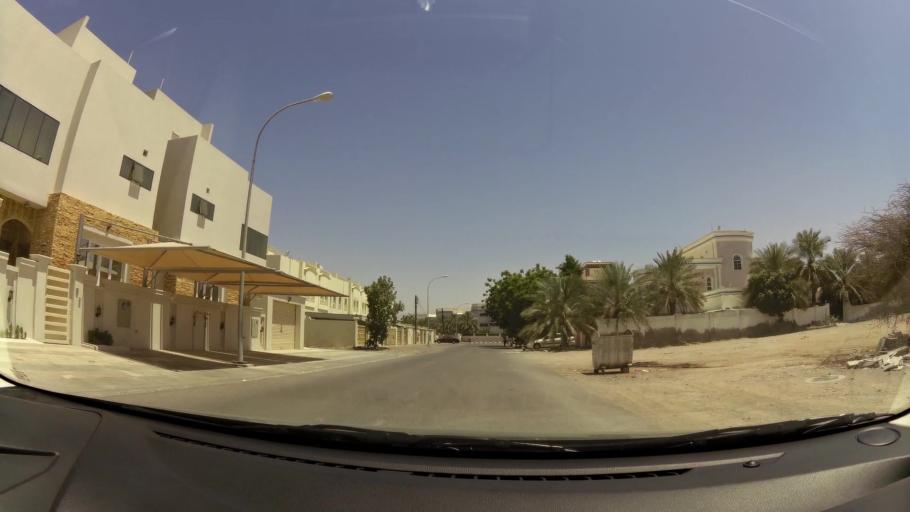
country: OM
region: Muhafazat Masqat
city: As Sib al Jadidah
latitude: 23.6188
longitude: 58.2302
